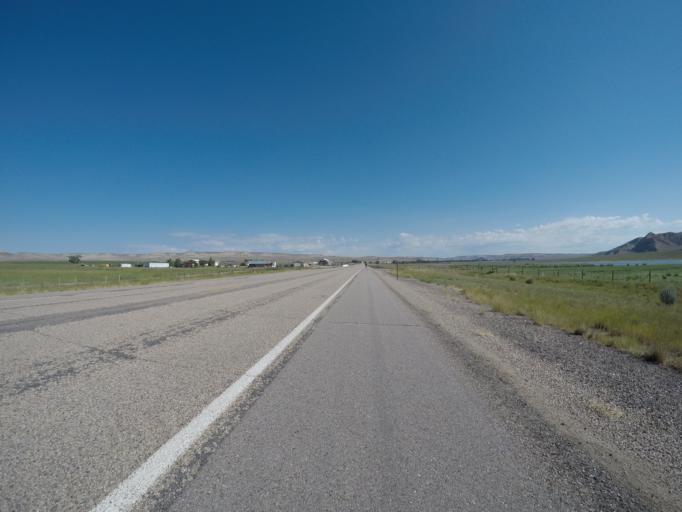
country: US
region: Wyoming
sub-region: Sublette County
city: Marbleton
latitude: 42.1492
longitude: -110.1860
